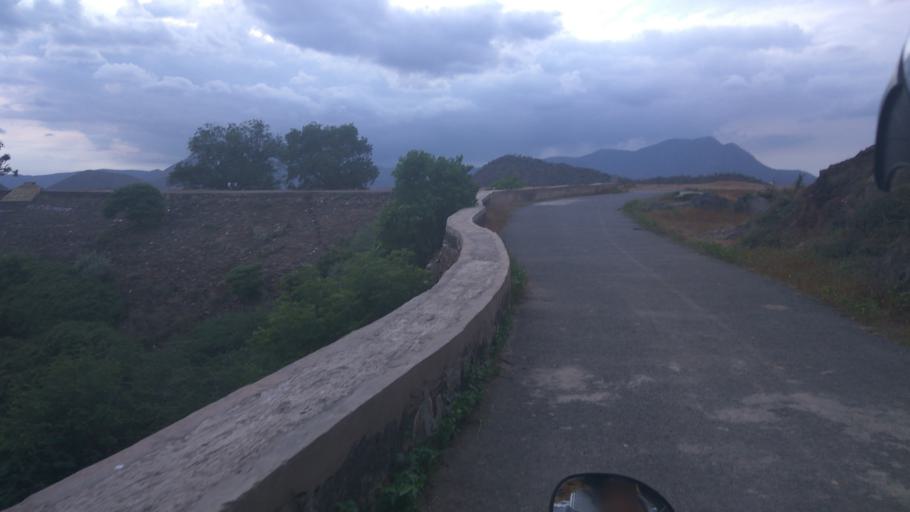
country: IN
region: Andhra Pradesh
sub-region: Prakasam
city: Cumbum
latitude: 15.5772
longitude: 79.0830
